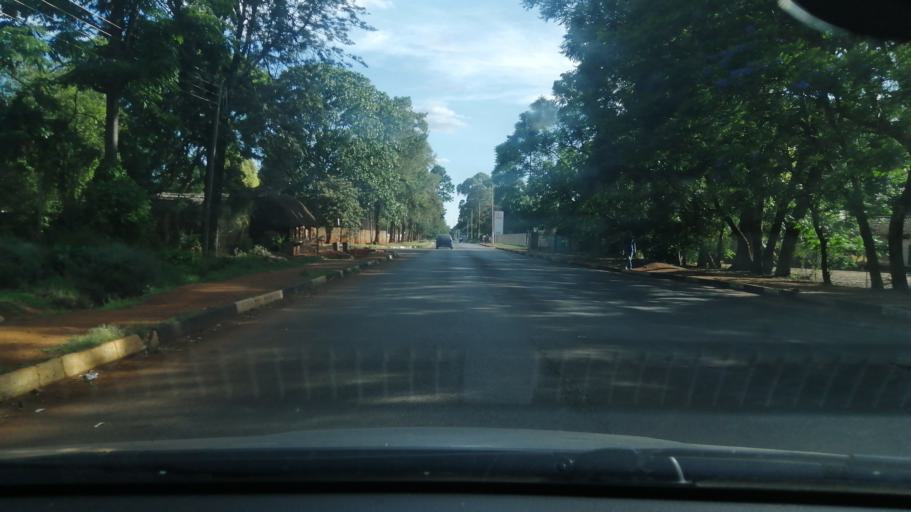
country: ZW
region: Harare
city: Harare
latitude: -17.7638
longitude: 31.0517
